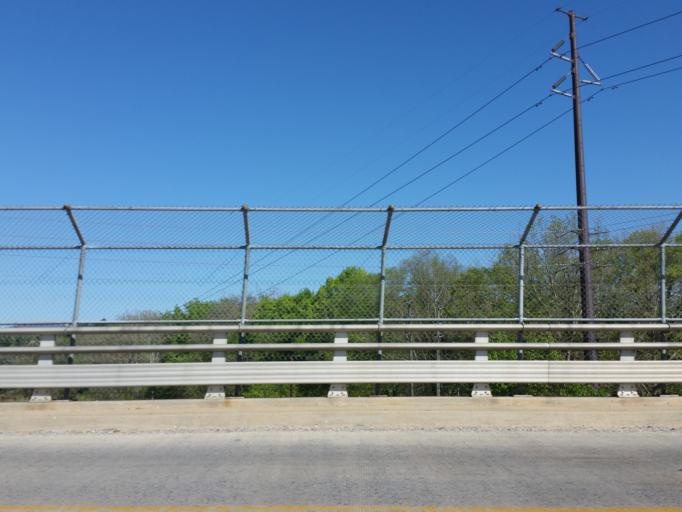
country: US
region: North Carolina
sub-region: Buncombe County
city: Asheville
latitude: 35.5644
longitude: -82.5572
